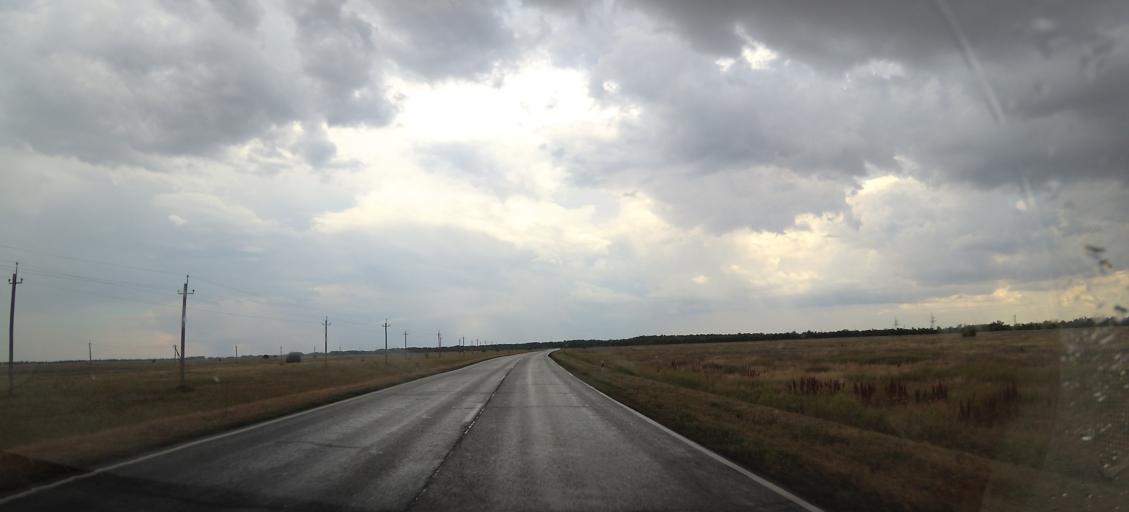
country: RU
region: Rostov
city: Zimovniki
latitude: 47.2938
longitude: 42.6045
